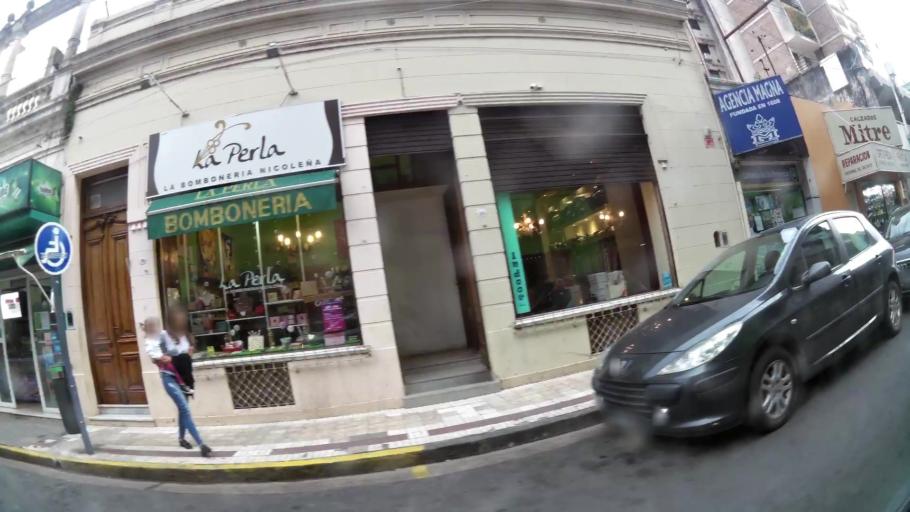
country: AR
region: Buenos Aires
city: San Nicolas de los Arroyos
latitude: -33.3286
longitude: -60.2170
